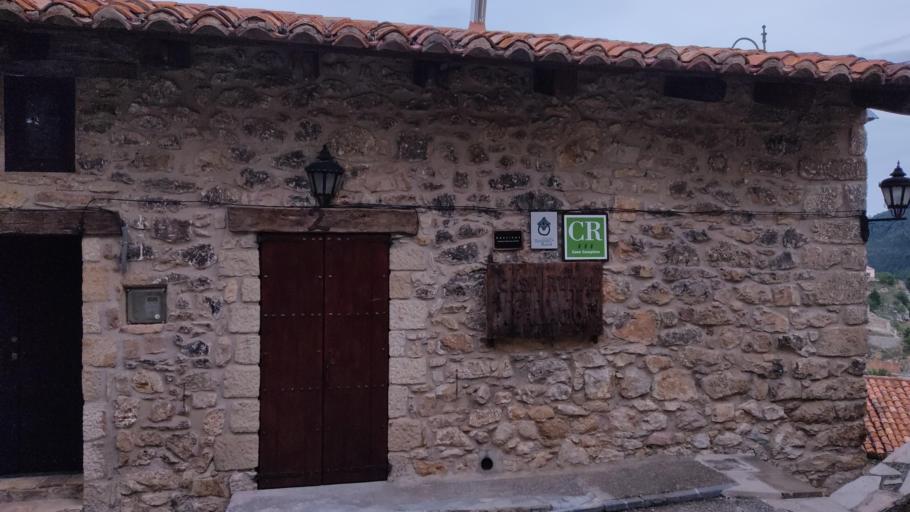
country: ES
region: Aragon
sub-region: Provincia de Teruel
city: Linares de Mora
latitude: 40.3221
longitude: -0.5747
